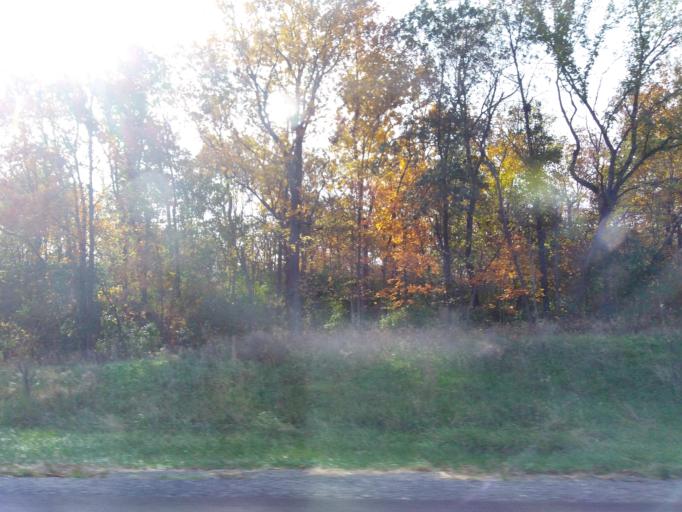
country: US
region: Illinois
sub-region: Madison County
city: Highland
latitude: 38.7864
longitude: -89.6585
